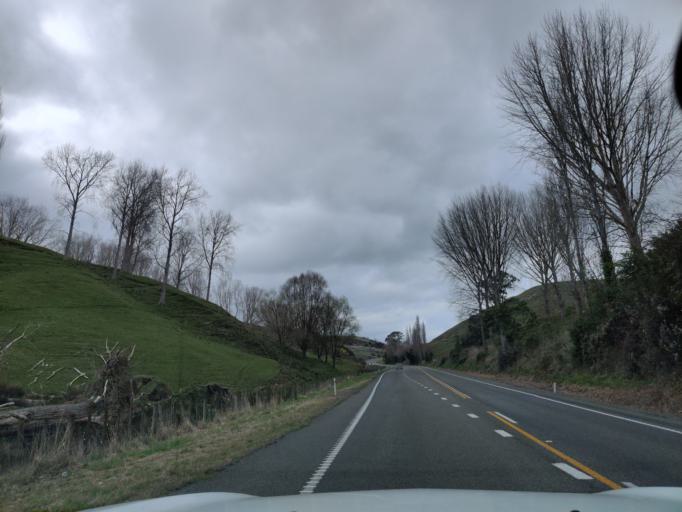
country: NZ
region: Manawatu-Wanganui
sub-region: Rangitikei District
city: Bulls
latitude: -39.9231
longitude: 175.5986
